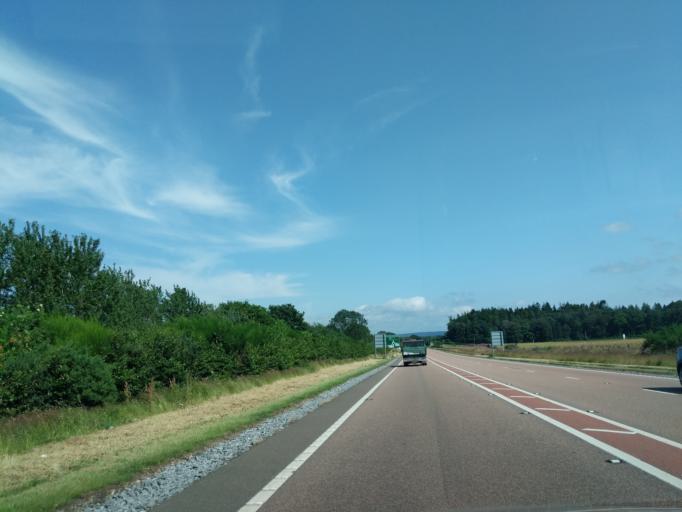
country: GB
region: Scotland
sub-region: Moray
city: Fochabers
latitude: 57.6229
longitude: -3.1235
